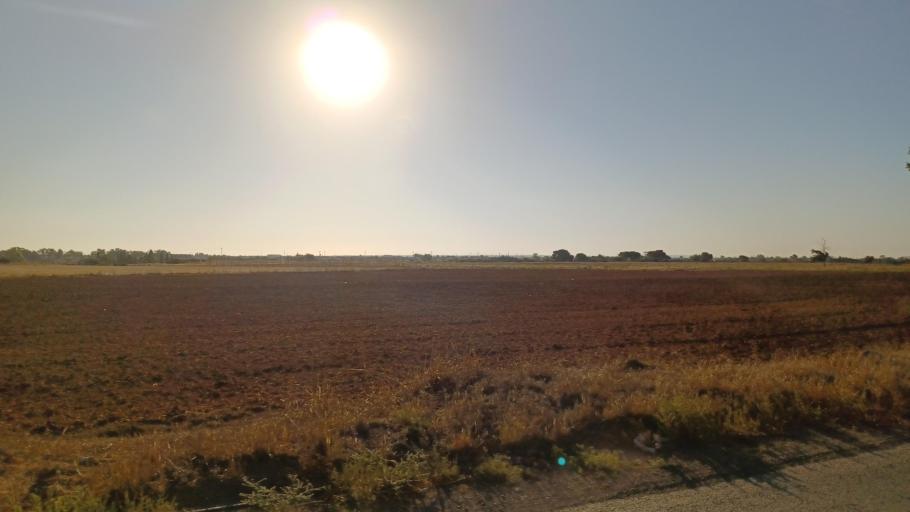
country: CY
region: Ammochostos
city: Achna
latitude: 35.0364
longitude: 33.7933
